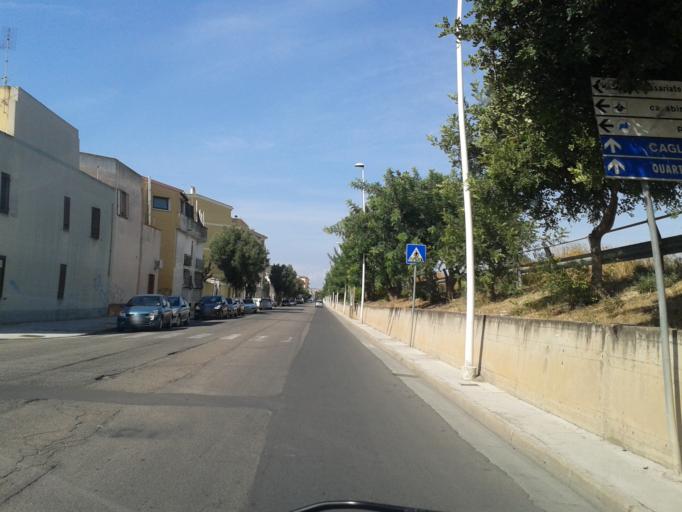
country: IT
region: Sardinia
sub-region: Provincia di Cagliari
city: Quartucciu
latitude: 39.2486
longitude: 9.1890
